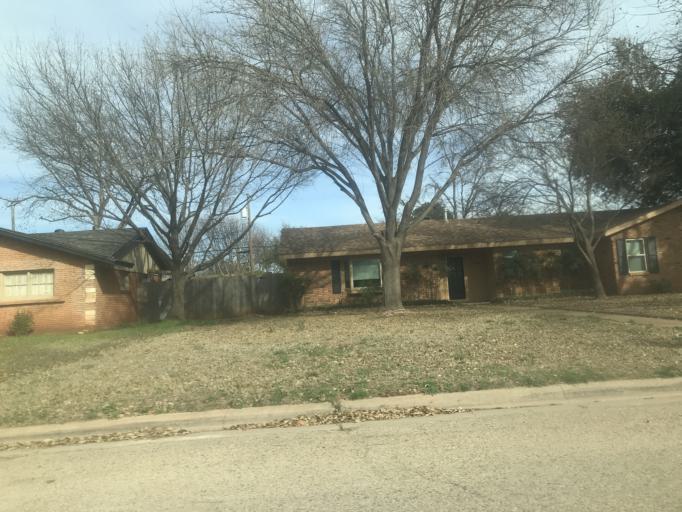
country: US
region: Texas
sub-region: Taylor County
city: Abilene
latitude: 32.4217
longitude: -99.7719
